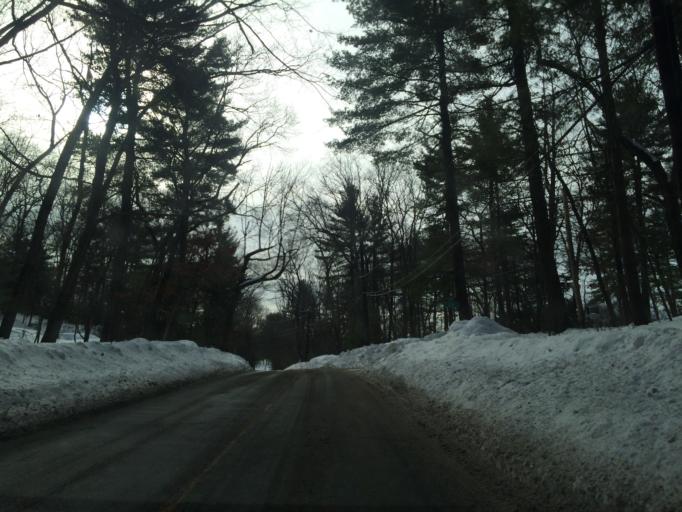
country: US
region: Massachusetts
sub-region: Middlesex County
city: Weston
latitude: 42.3586
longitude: -71.2727
